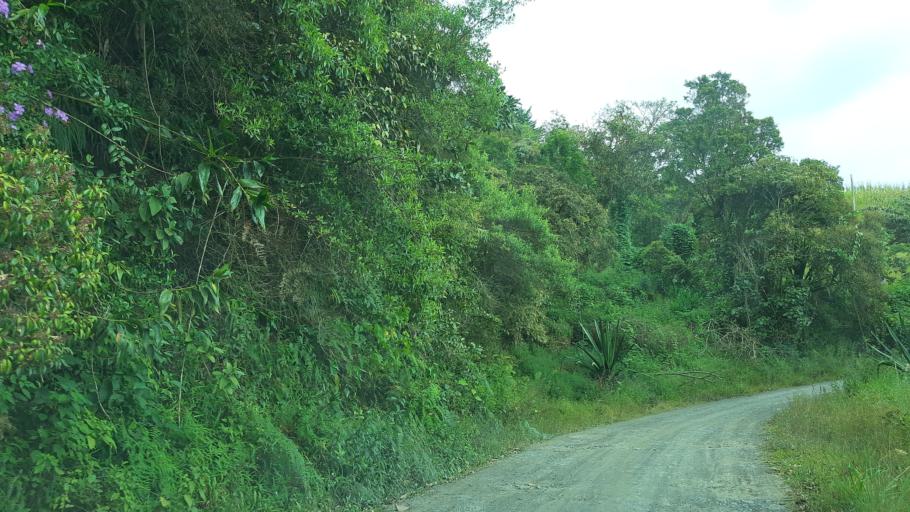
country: CO
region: Boyaca
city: Garagoa
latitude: 5.0074
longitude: -73.3412
